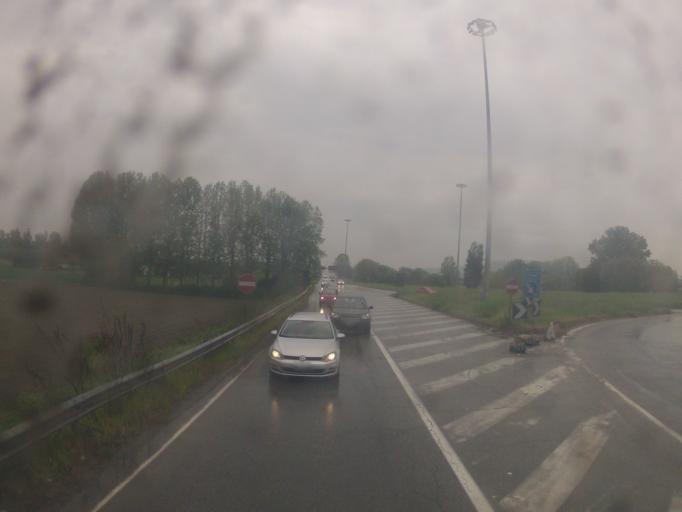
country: IT
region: Piedmont
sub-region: Provincia di Torino
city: La Loggia
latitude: 44.9666
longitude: 7.6694
